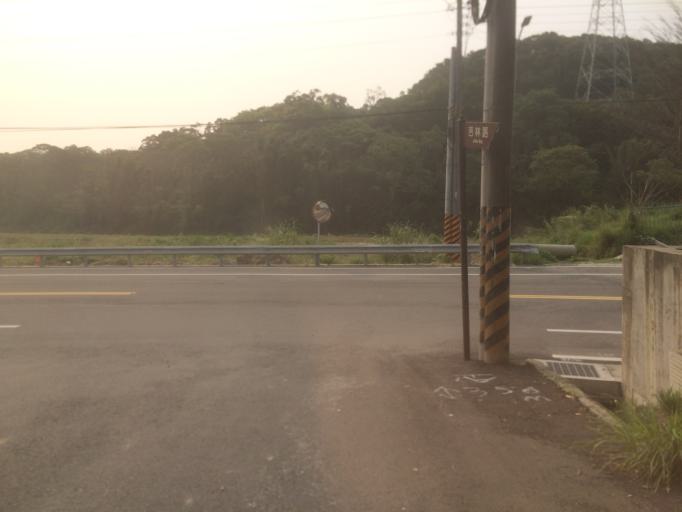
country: TW
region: Taiwan
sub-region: Hsinchu
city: Hsinchu
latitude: 24.7604
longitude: 120.9791
